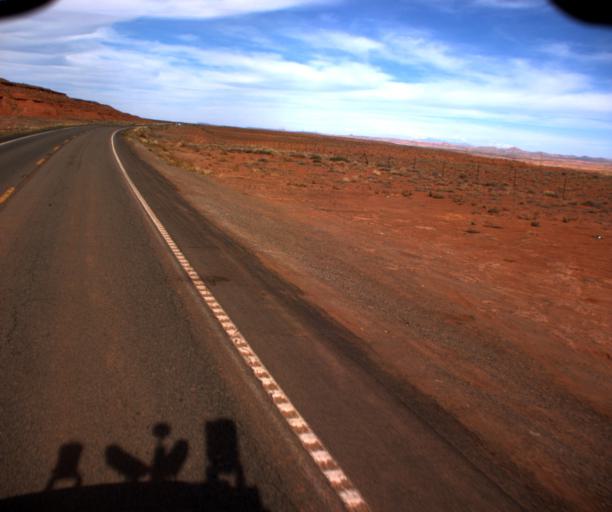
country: US
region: Arizona
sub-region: Navajo County
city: Kayenta
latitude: 36.9044
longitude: -109.7884
